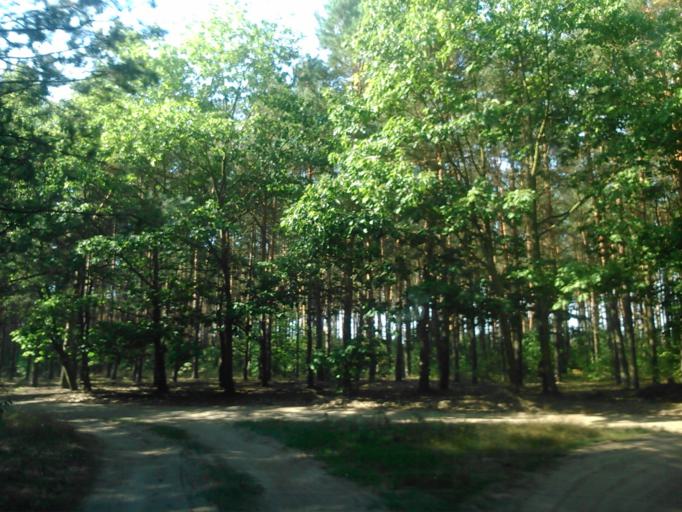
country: PL
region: Kujawsko-Pomorskie
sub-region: Powiat golubsko-dobrzynski
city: Golub-Dobrzyn
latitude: 53.1176
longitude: 19.0887
